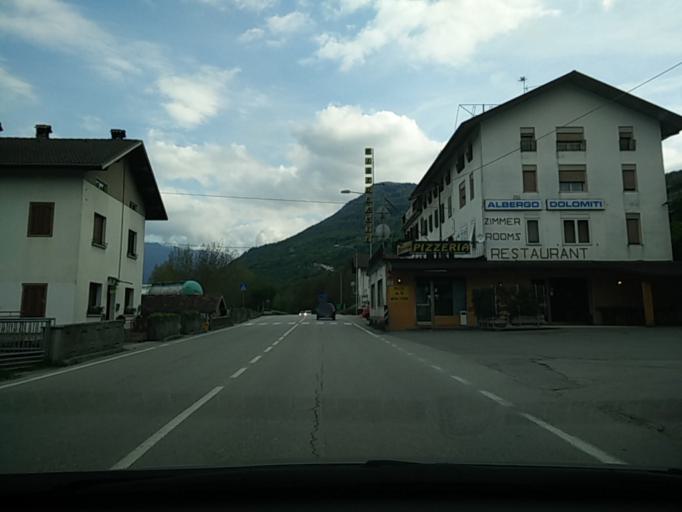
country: IT
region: Veneto
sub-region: Provincia di Belluno
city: Farra d'Alpago
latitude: 46.1361
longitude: 12.3168
